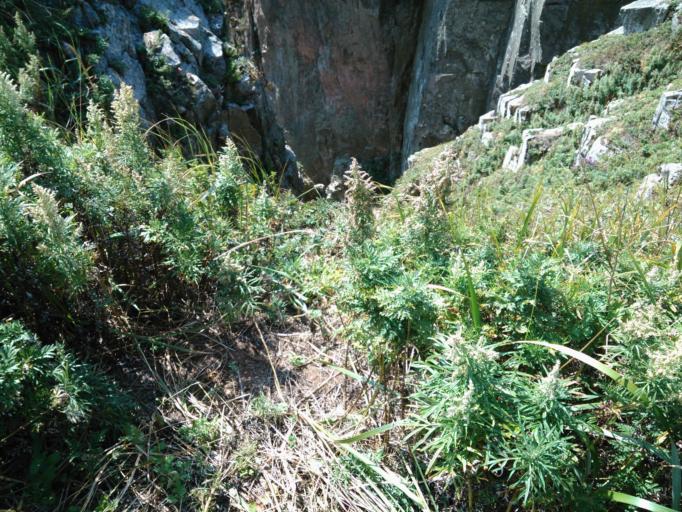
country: RU
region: Primorskiy
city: Russkiy
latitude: 42.9329
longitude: 131.8241
